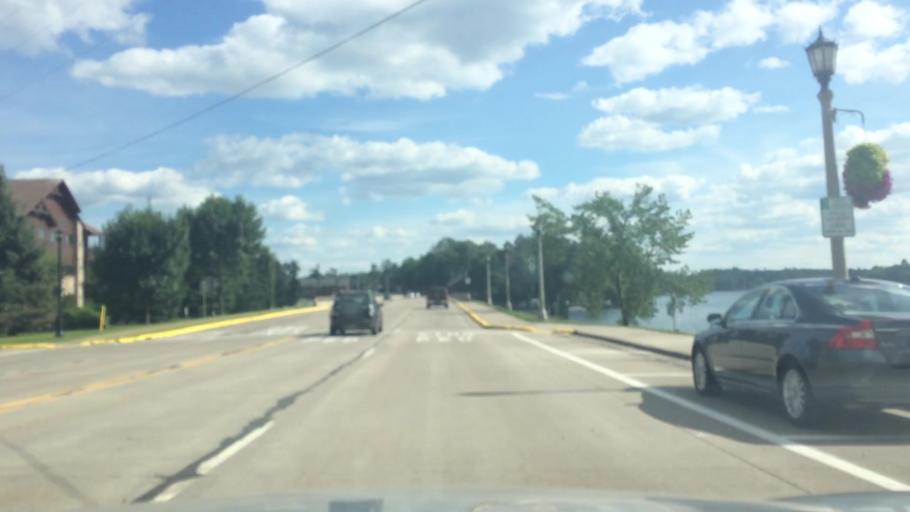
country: US
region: Wisconsin
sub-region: Vilas County
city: Lac du Flambeau
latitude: 45.8684
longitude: -89.7095
